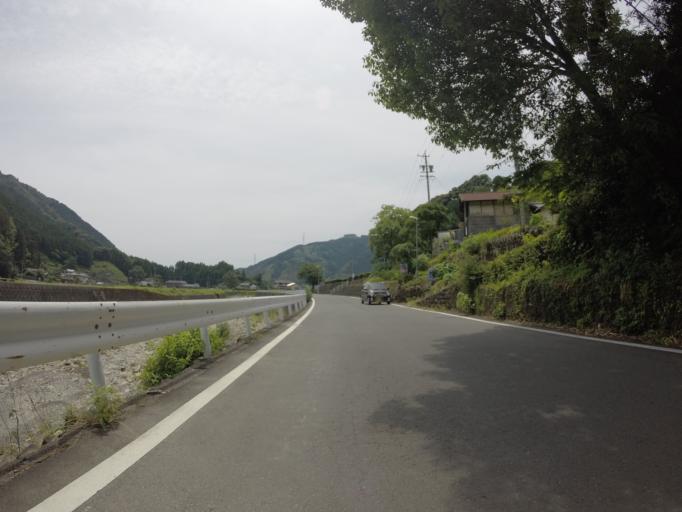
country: JP
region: Shizuoka
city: Shizuoka-shi
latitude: 35.0156
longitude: 138.2805
